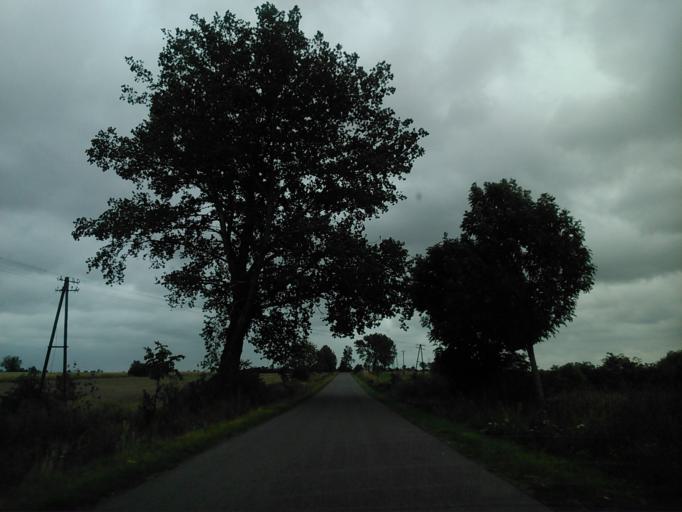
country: PL
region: Greater Poland Voivodeship
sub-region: Powiat koninski
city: Skulsk
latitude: 52.5596
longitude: 18.3969
